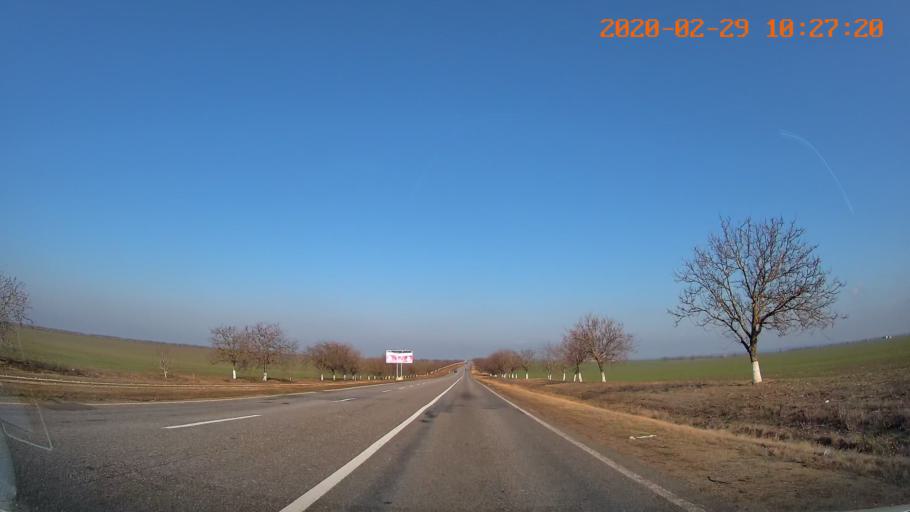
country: MD
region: Telenesti
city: Tiraspolul Nou
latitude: 46.8945
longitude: 29.5984
